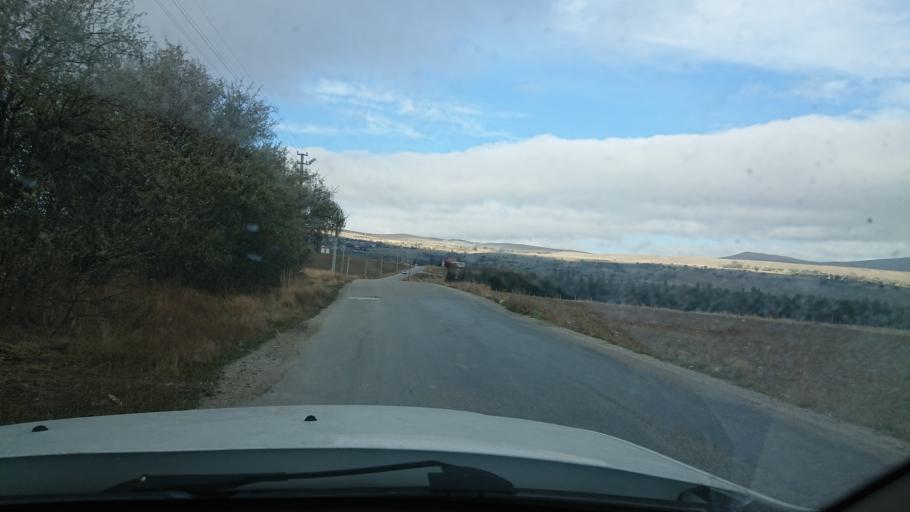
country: TR
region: Aksaray
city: Ortakoy
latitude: 38.7478
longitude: 34.0280
